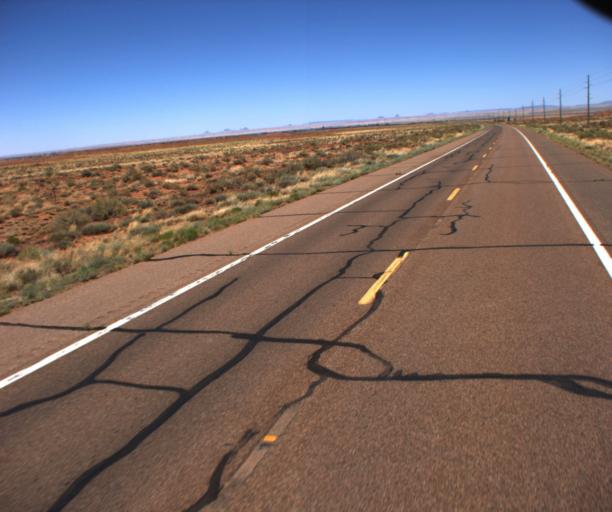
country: US
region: Arizona
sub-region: Coconino County
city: LeChee
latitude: 34.9667
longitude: -110.7344
